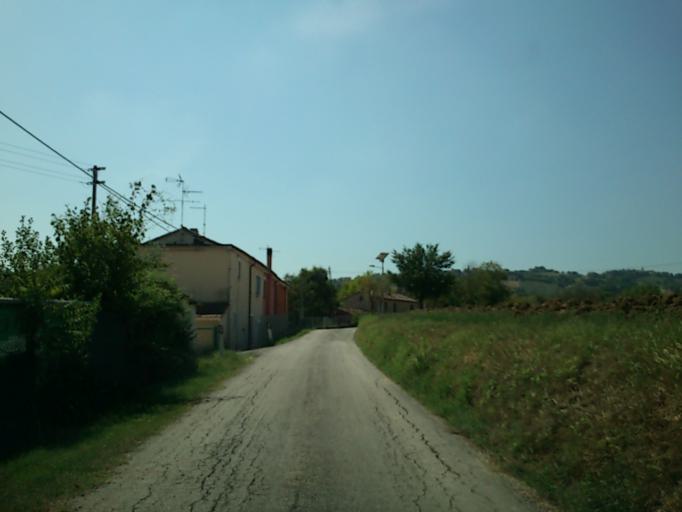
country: IT
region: The Marches
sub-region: Provincia di Pesaro e Urbino
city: Lucrezia
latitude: 43.7785
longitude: 12.9174
